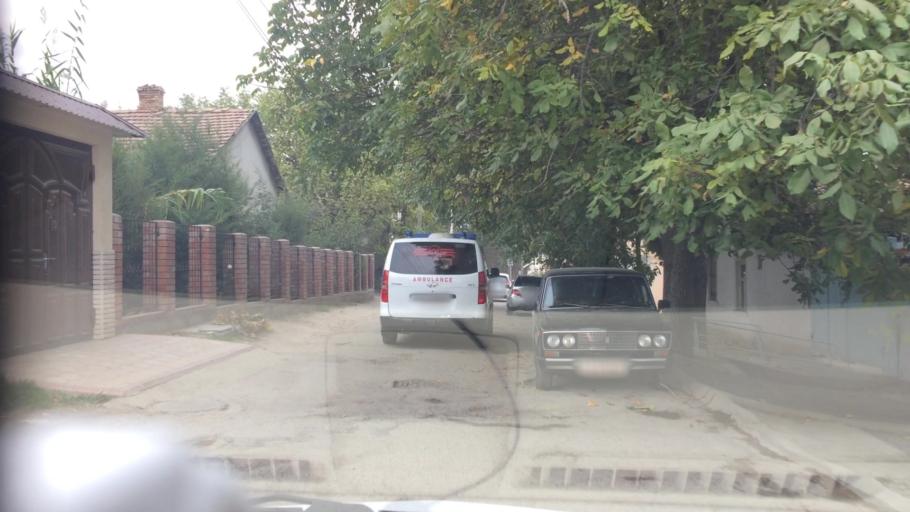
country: UZ
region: Toshkent
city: Salor
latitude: 41.3079
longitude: 69.3352
